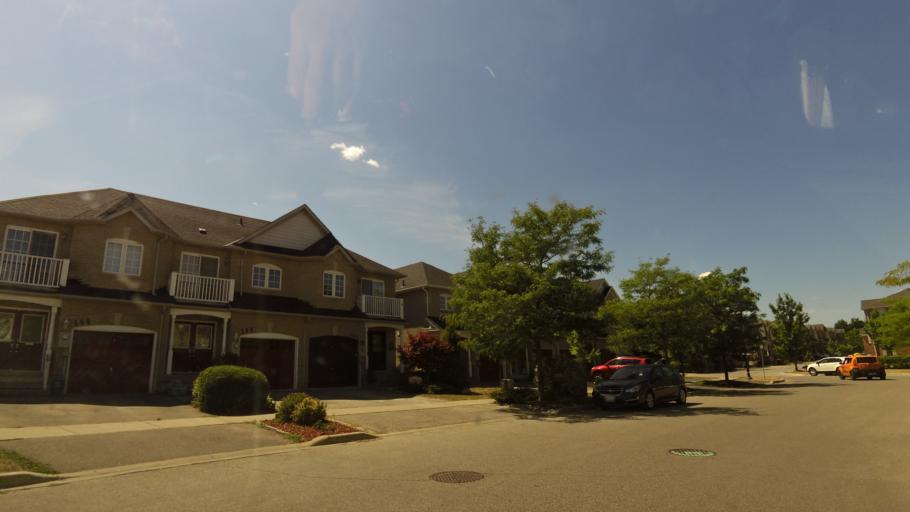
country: CA
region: Ontario
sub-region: Halton
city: Milton
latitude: 43.6534
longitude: -79.9087
